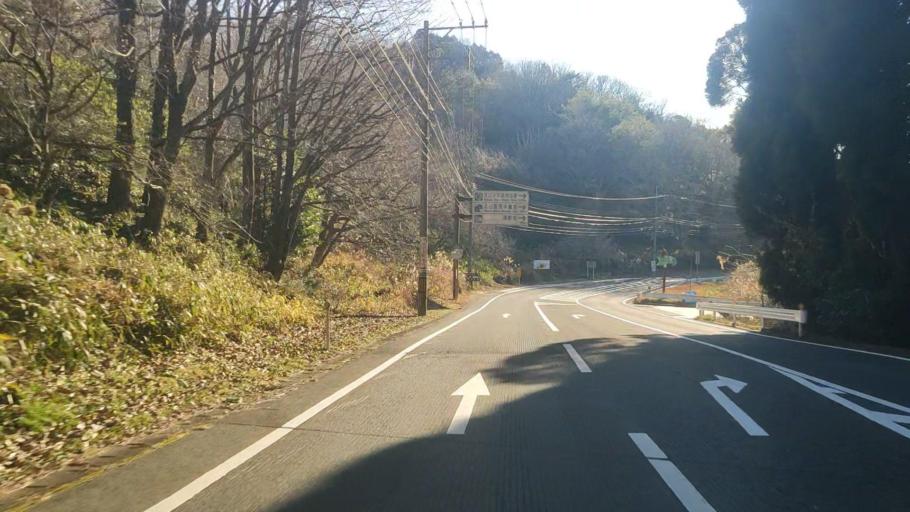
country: JP
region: Saga Prefecture
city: Kanzakimachi-kanzaki
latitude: 33.4120
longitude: 130.2750
